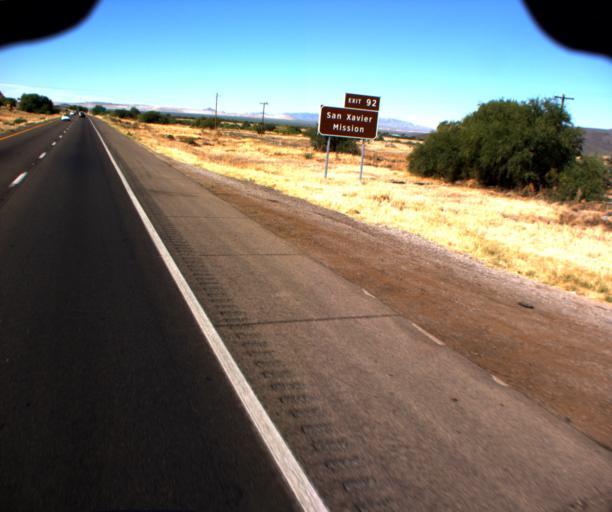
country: US
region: Arizona
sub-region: Pima County
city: Drexel Heights
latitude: 32.1159
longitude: -110.9905
